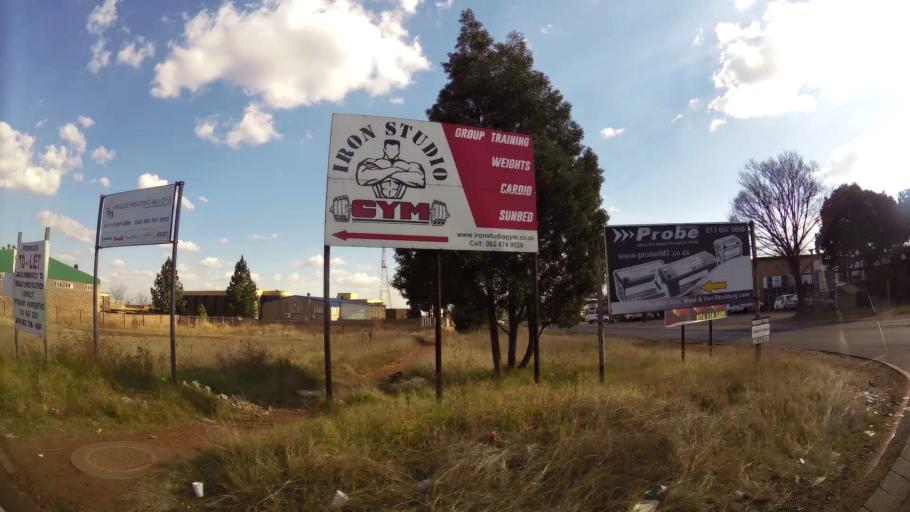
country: ZA
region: Mpumalanga
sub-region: Nkangala District Municipality
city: Witbank
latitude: -25.9007
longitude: 29.2287
